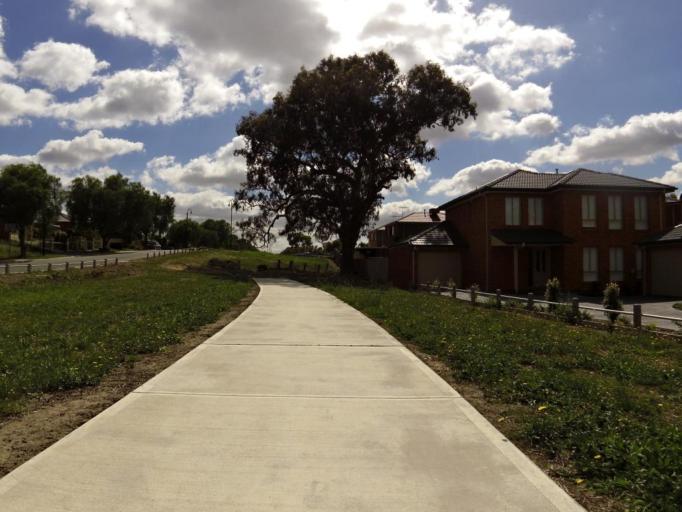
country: AU
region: Victoria
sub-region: Whittlesea
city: Mernda
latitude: -37.6298
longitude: 145.0892
